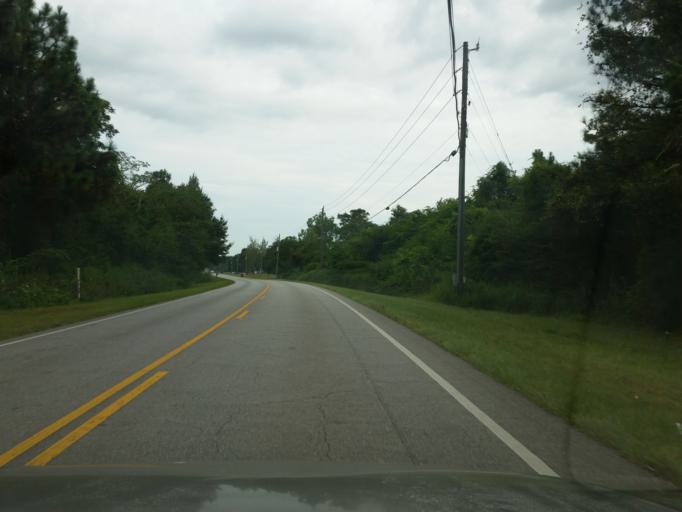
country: US
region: Florida
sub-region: Escambia County
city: Molino
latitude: 30.6964
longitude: -87.3323
